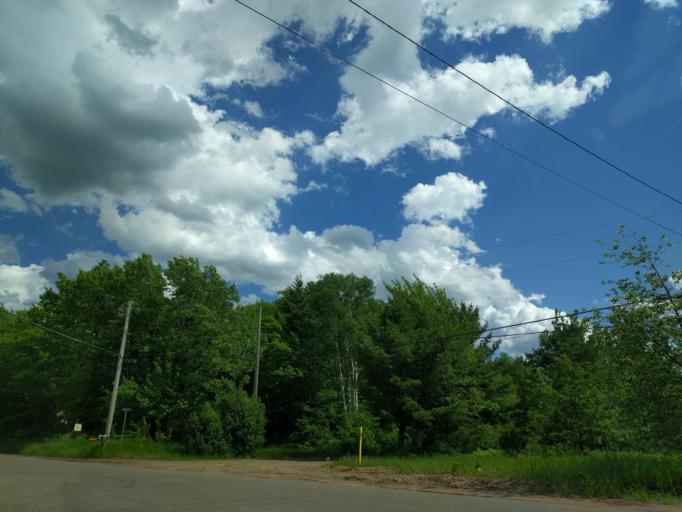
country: US
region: Michigan
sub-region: Marquette County
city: Trowbridge Park
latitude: 46.5408
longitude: -87.5131
